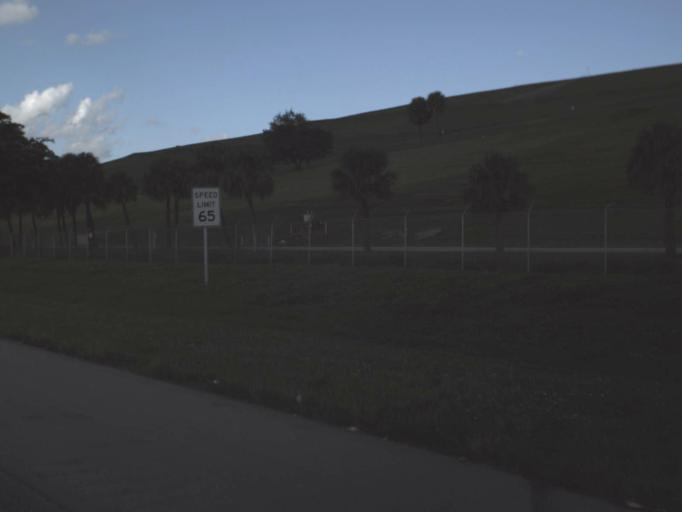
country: US
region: Florida
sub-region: Broward County
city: Coconut Creek
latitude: 26.2826
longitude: -80.1689
